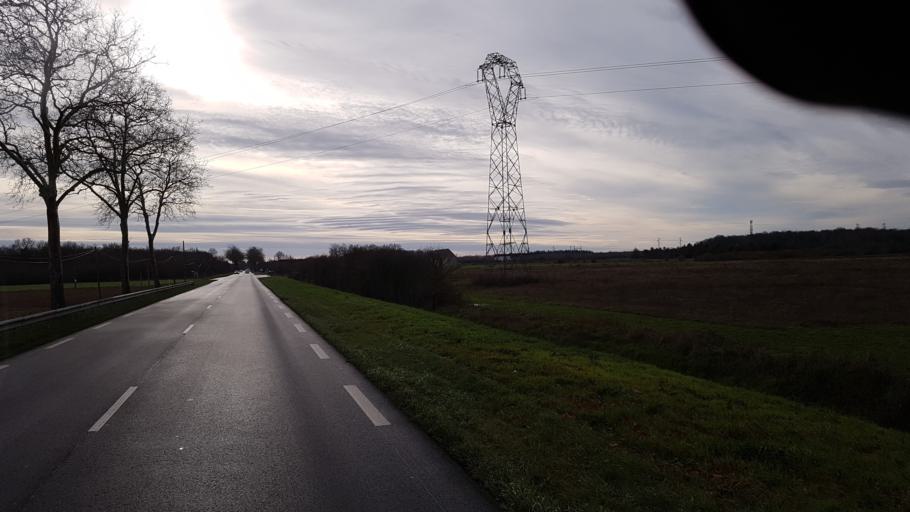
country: FR
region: Centre
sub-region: Departement du Loiret
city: Saint-Cyr-en-Val
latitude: 47.8005
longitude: 1.9312
